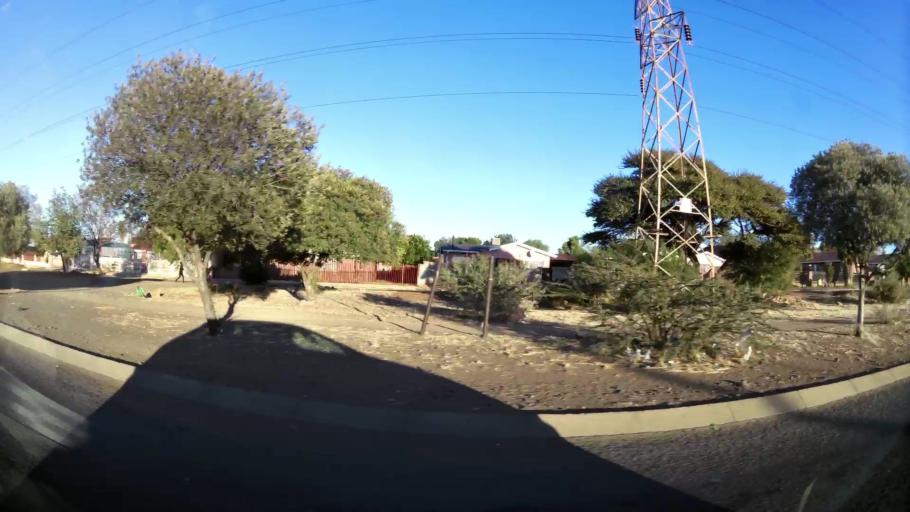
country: ZA
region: Northern Cape
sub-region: Frances Baard District Municipality
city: Kimberley
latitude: -28.7701
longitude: 24.7645
